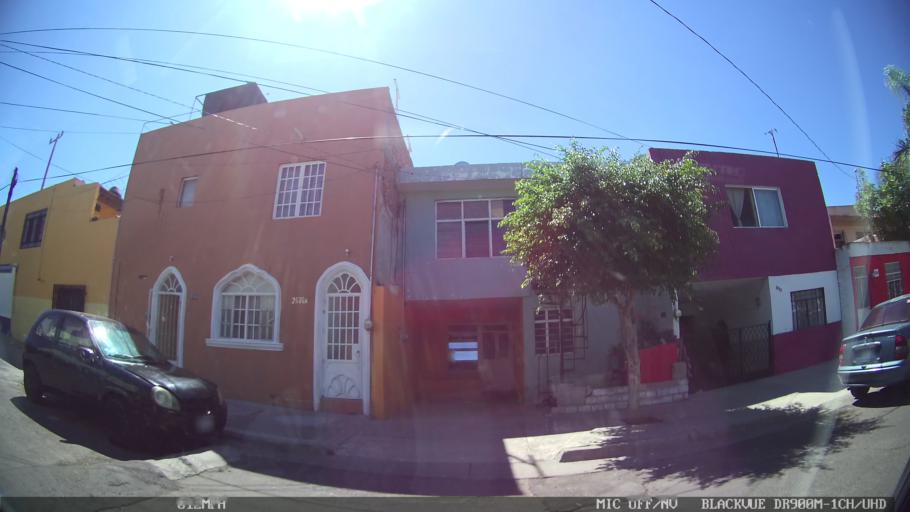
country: MX
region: Jalisco
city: Tlaquepaque
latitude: 20.6898
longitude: -103.2817
